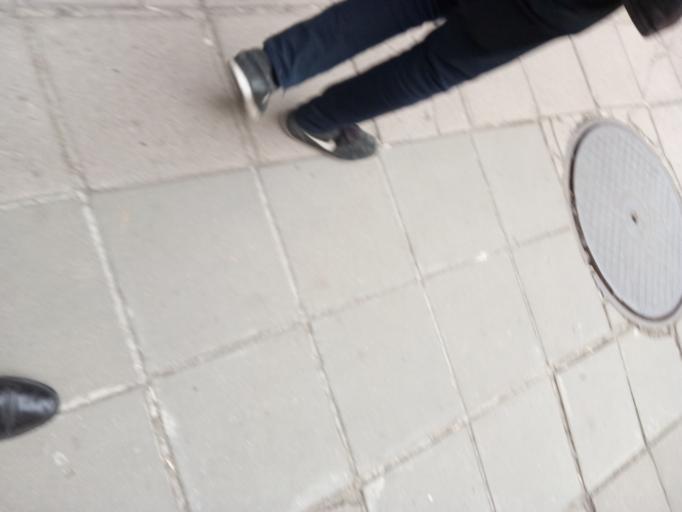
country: BG
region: Sofia-Capital
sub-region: Stolichna Obshtina
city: Sofia
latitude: 42.6927
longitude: 23.3197
